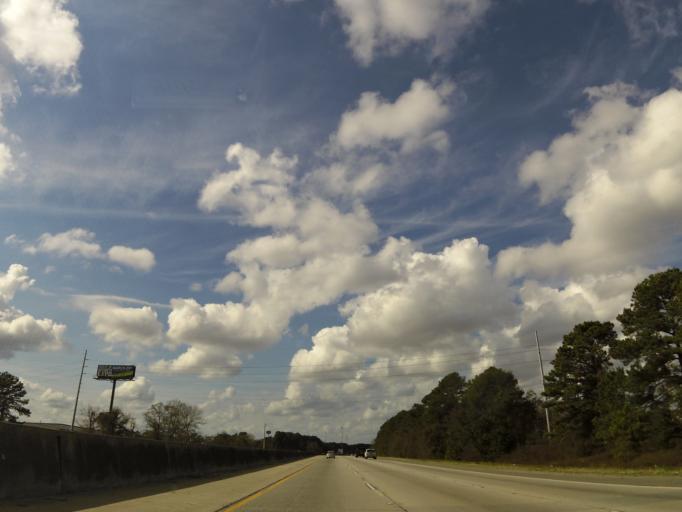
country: US
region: South Carolina
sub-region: Charleston County
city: North Charleston
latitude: 32.8674
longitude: -80.0030
